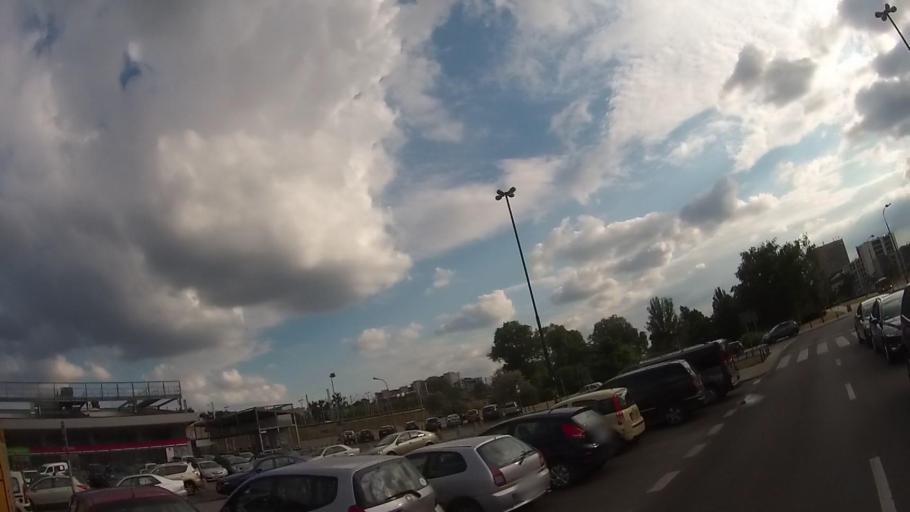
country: PL
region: Masovian Voivodeship
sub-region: Warszawa
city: Praga Polnoc
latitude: 52.2524
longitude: 21.0501
